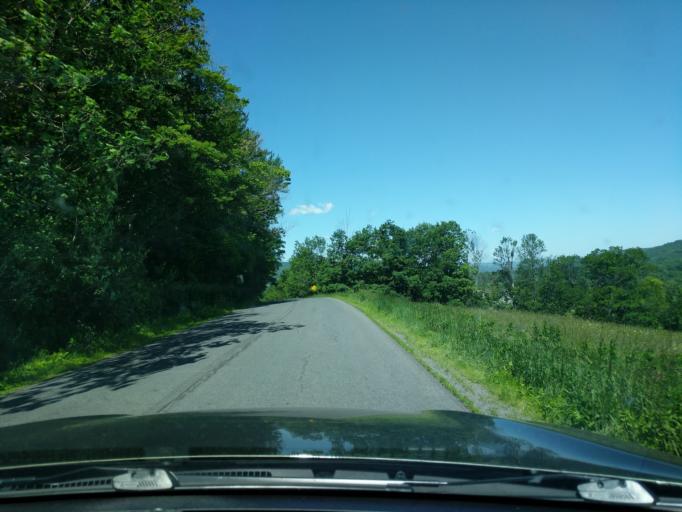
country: US
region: New York
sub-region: Tompkins County
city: East Ithaca
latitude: 42.3807
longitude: -76.3684
